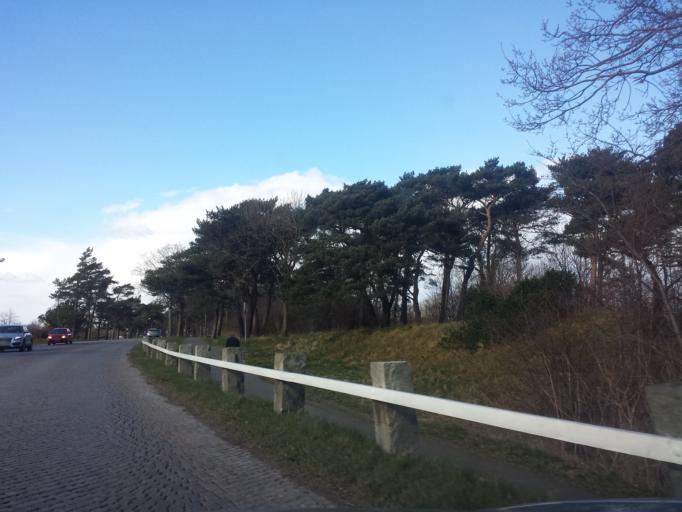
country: SE
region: Skane
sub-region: Simrishamns Kommun
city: Simrishamn
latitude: 55.5633
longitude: 14.3370
